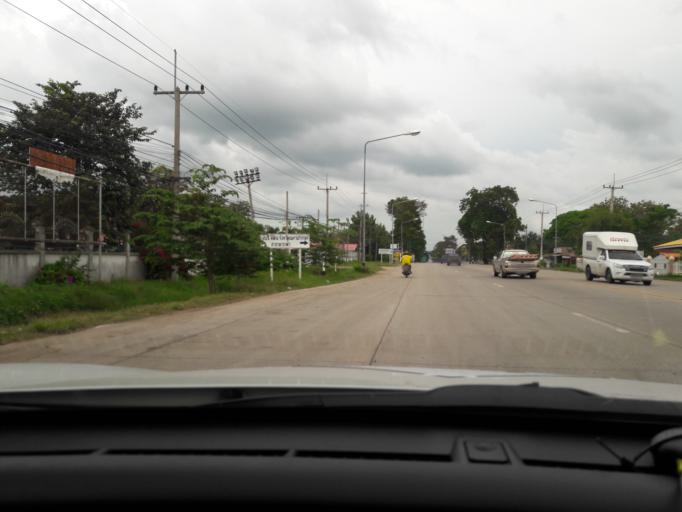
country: TH
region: Nakhon Sawan
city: Tak Fa
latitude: 15.3477
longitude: 100.4954
